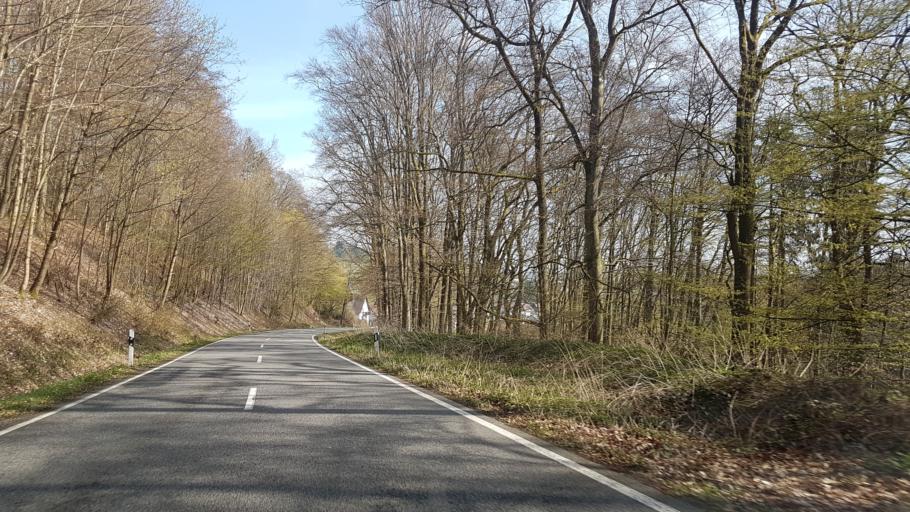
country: DE
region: Rheinland-Pfalz
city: Altenkirchen
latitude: 49.4385
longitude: 7.3062
